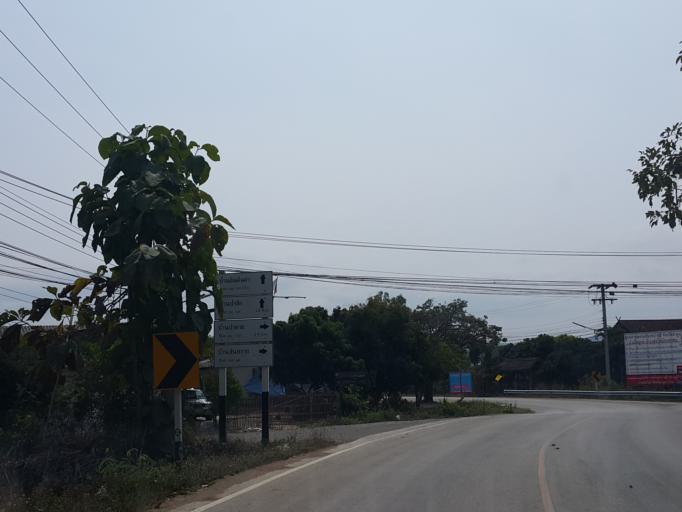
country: TH
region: Lamphun
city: Ban Thi
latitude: 18.6621
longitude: 99.1053
